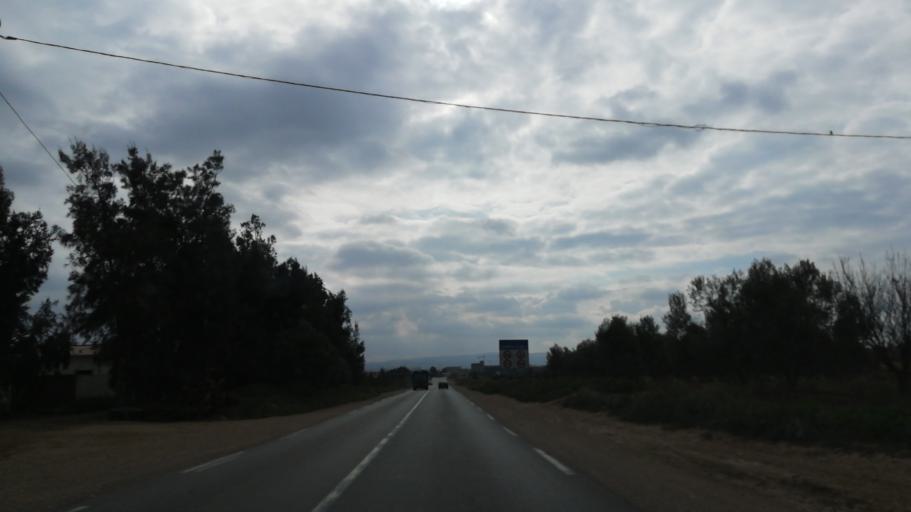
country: DZ
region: Oran
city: Sidi ech Chahmi
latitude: 35.5714
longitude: -0.4506
